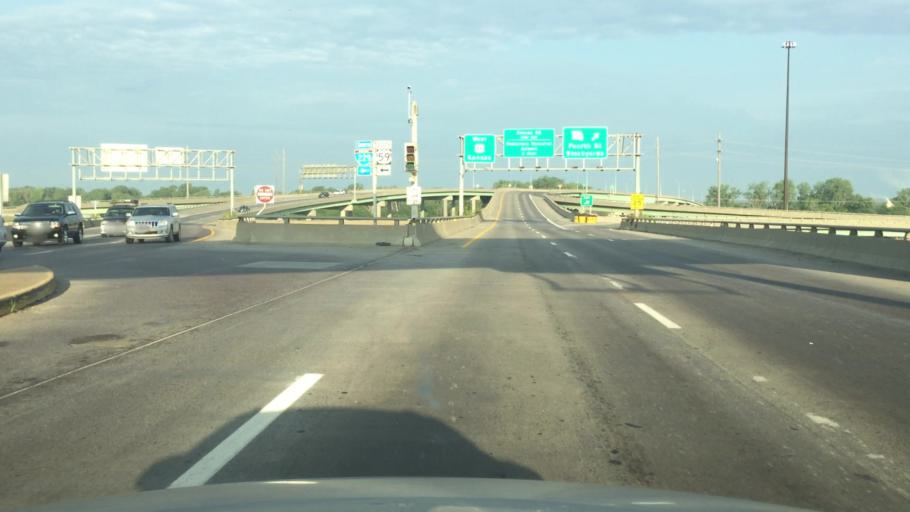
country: US
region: Kansas
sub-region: Doniphan County
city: Elwood
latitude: 39.7488
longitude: -94.8536
